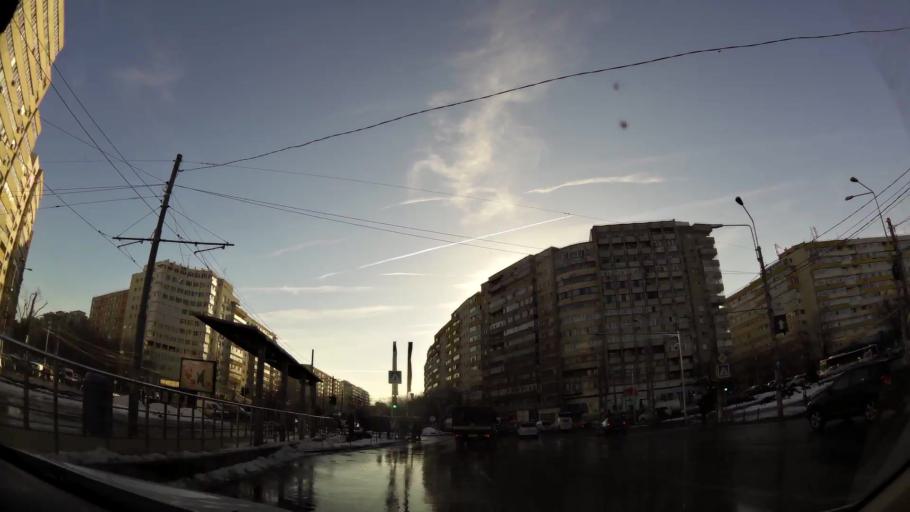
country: RO
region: Ilfov
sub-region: Comuna Fundeni-Dobroesti
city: Fundeni
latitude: 44.4627
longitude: 26.1333
